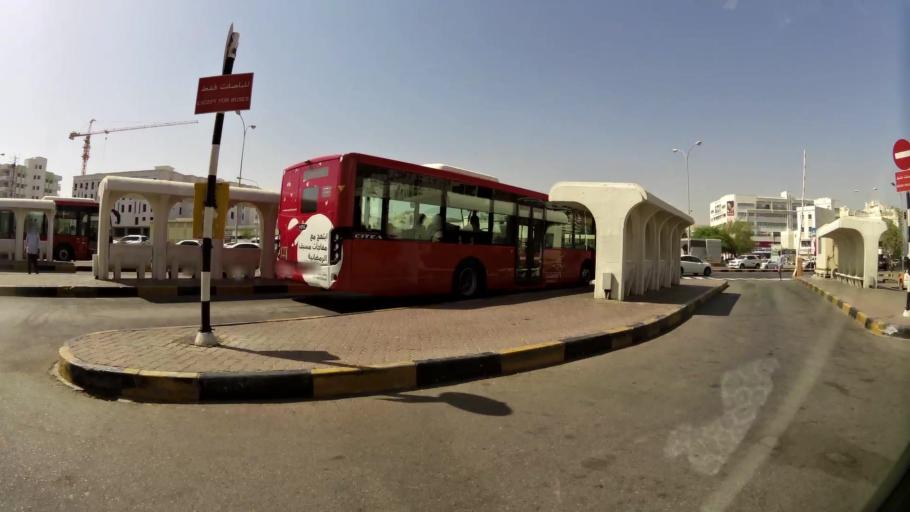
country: OM
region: Muhafazat Masqat
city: Muscat
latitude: 23.5952
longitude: 58.5453
